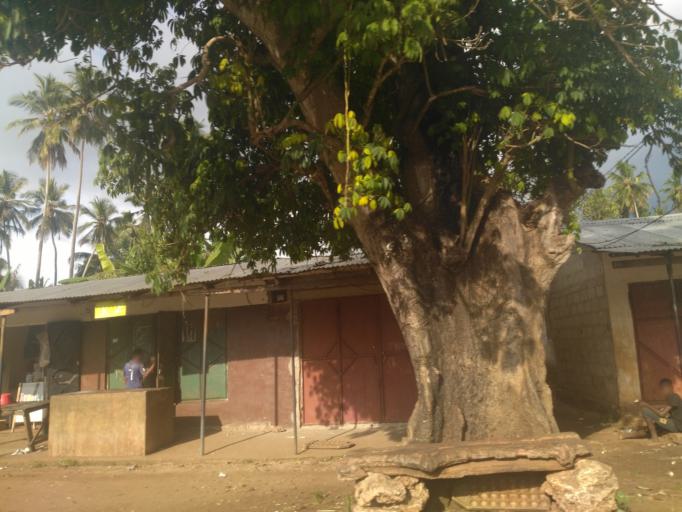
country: TZ
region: Zanzibar Central/South
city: Koani
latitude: -6.1113
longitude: 39.3019
